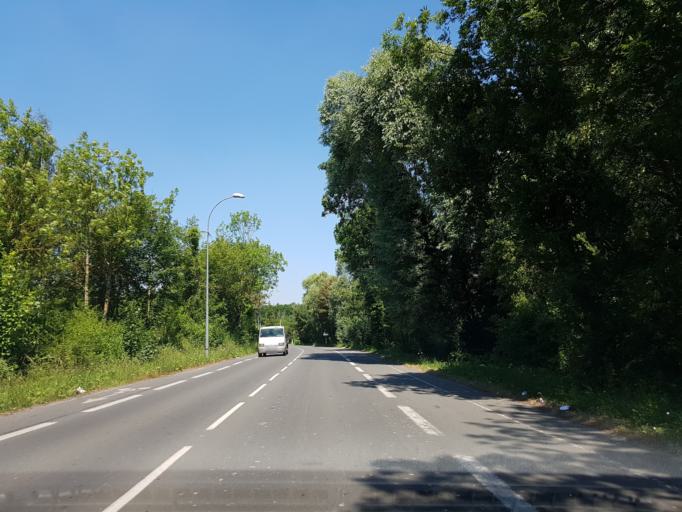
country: FR
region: Nord-Pas-de-Calais
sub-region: Departement du Nord
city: Neuville-sur-Escaut
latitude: 50.3036
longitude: 3.3491
